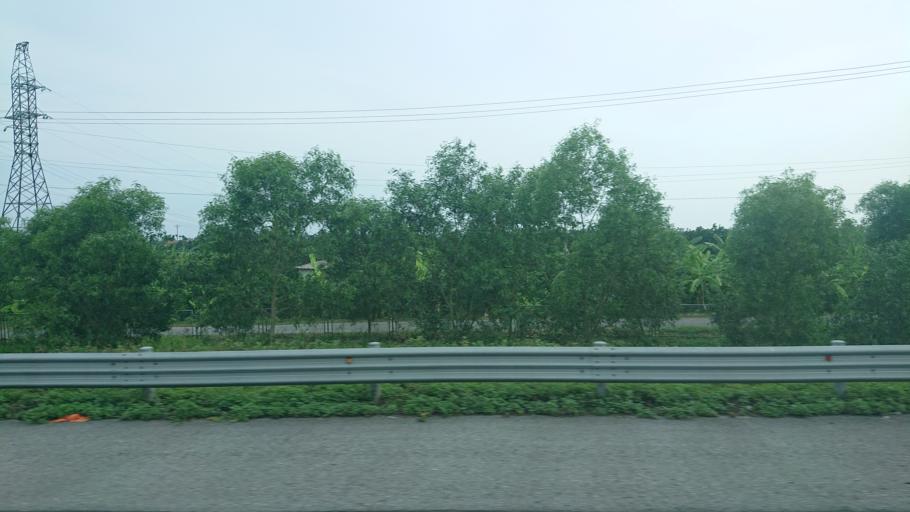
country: VN
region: Hai Duong
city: Tu Ky
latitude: 20.8306
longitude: 106.4483
